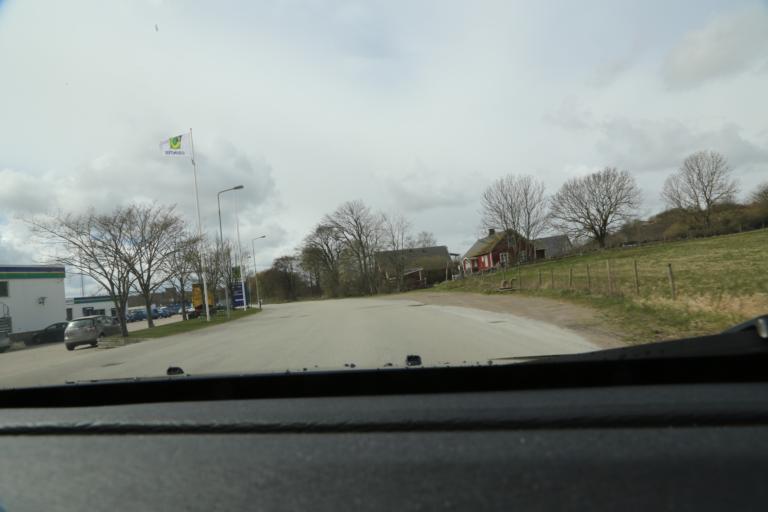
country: SE
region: Halland
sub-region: Varbergs Kommun
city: Varberg
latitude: 57.1271
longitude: 12.2800
